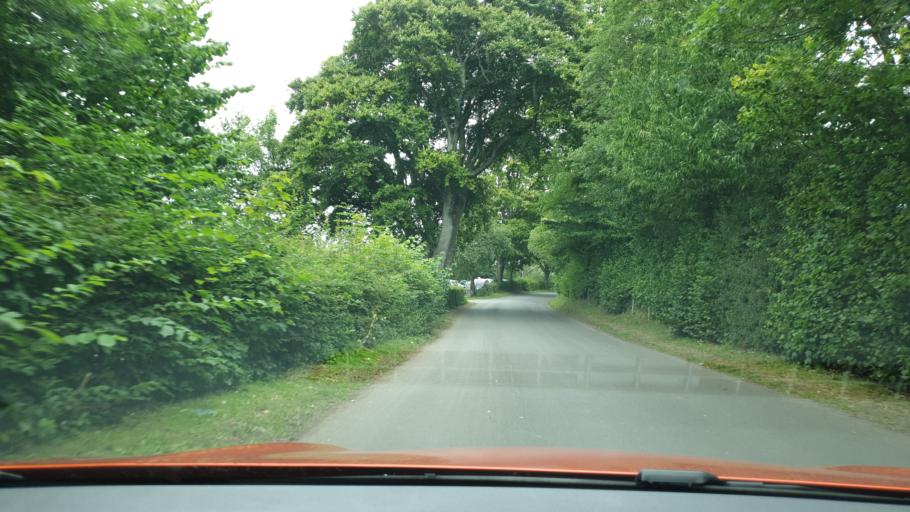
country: GB
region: England
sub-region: Cumbria
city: Penrith
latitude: 54.6044
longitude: -2.8234
